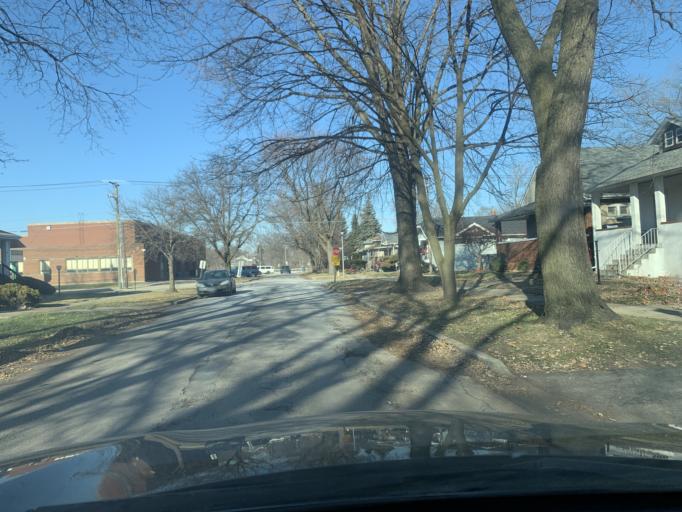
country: US
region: Illinois
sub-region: Cook County
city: Maywood
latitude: 41.8695
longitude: -87.8373
